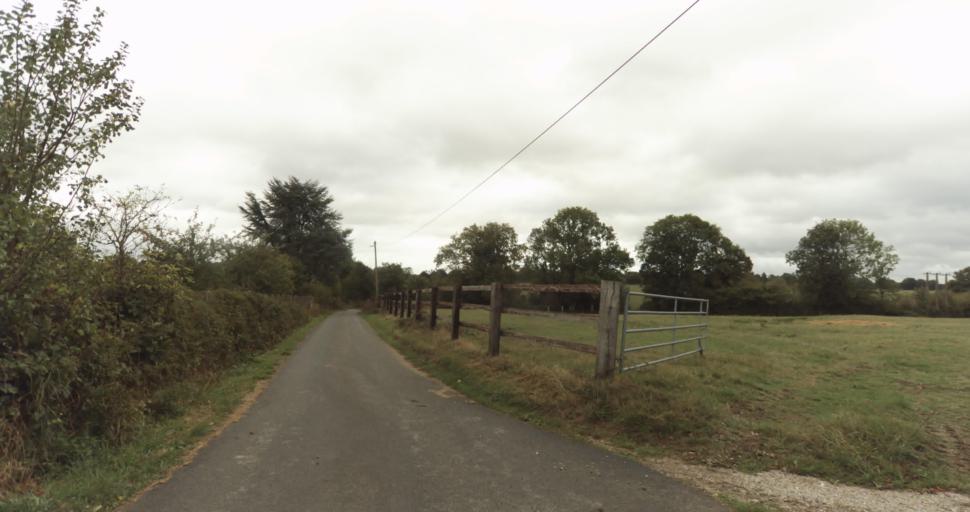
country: FR
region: Lower Normandy
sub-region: Departement de l'Orne
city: Sainte-Gauburge-Sainte-Colombe
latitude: 48.7256
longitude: 0.4700
